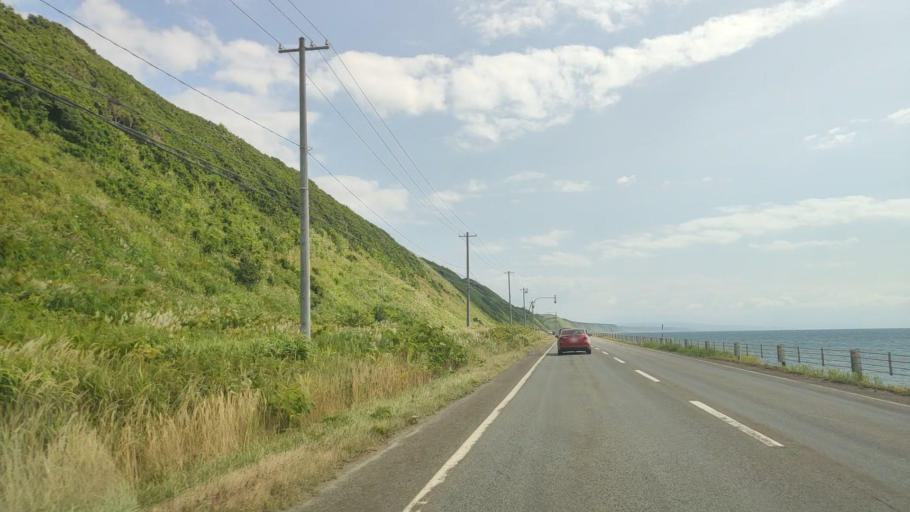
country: JP
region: Hokkaido
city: Rumoi
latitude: 44.0895
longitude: 141.6615
